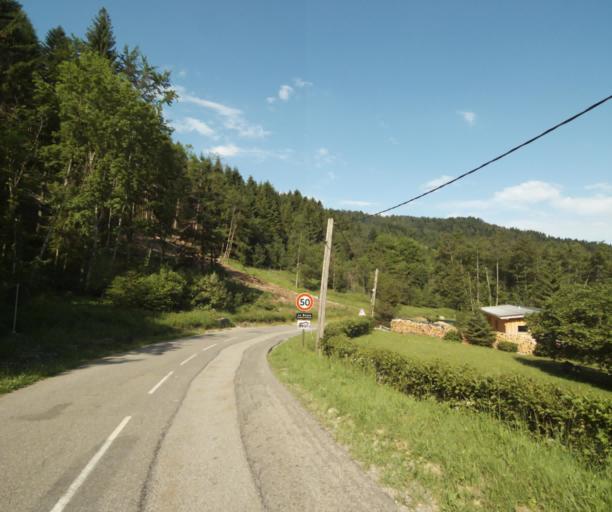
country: FR
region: Rhone-Alpes
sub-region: Departement de la Haute-Savoie
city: Lyaud
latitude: 46.2993
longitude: 6.5032
